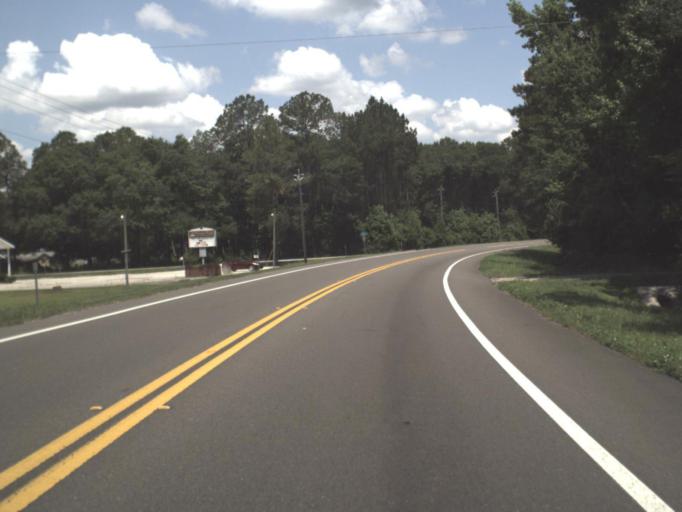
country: US
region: Florida
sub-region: Nassau County
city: Nassau Village-Ratliff
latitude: 30.5194
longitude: -81.7666
